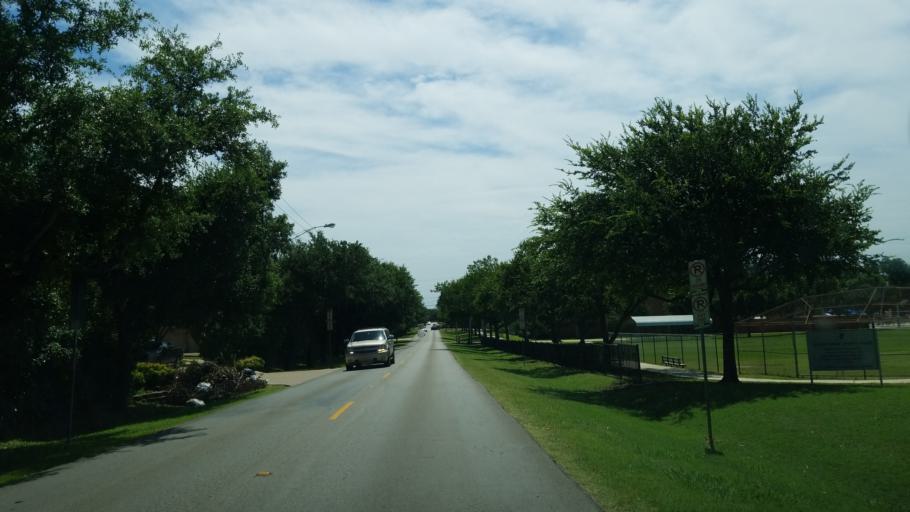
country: US
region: Texas
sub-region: Dallas County
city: Addison
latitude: 32.9022
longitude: -96.8370
